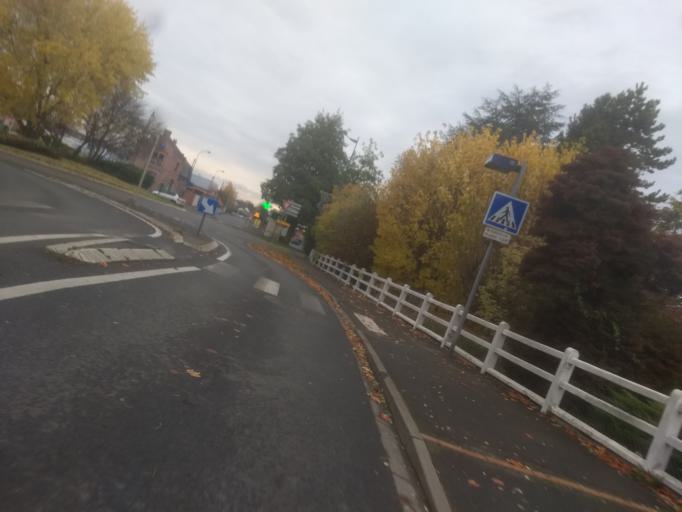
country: FR
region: Nord-Pas-de-Calais
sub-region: Departement du Pas-de-Calais
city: Achicourt
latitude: 50.2875
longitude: 2.7453
